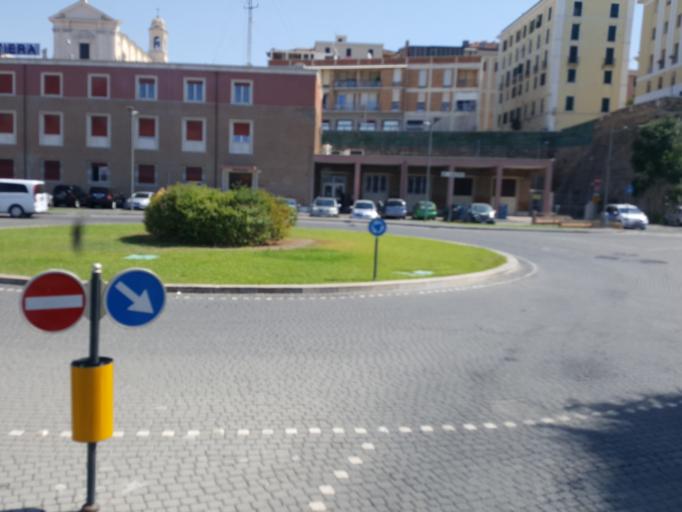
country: IT
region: Latium
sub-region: Citta metropolitana di Roma Capitale
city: Civitavecchia
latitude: 42.0913
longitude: 11.7907
